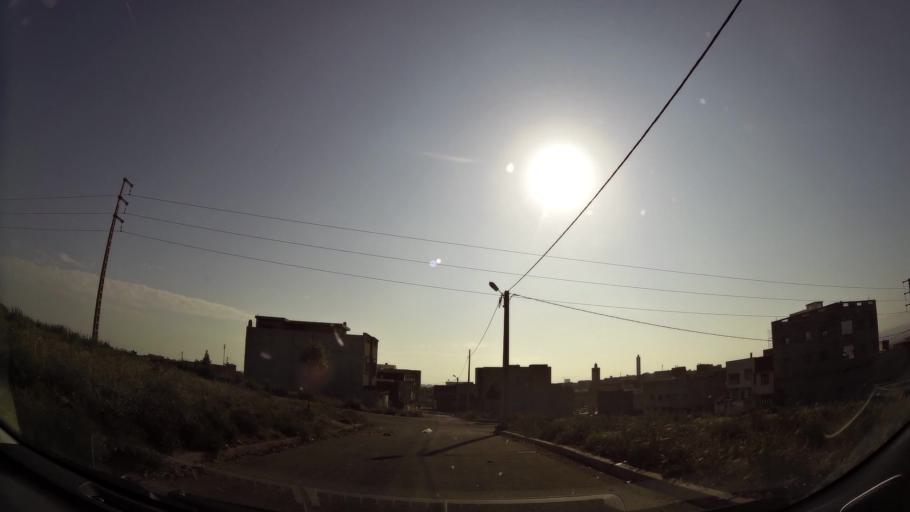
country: MA
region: Oriental
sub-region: Oujda-Angad
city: Oujda
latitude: 34.6767
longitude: -1.9461
